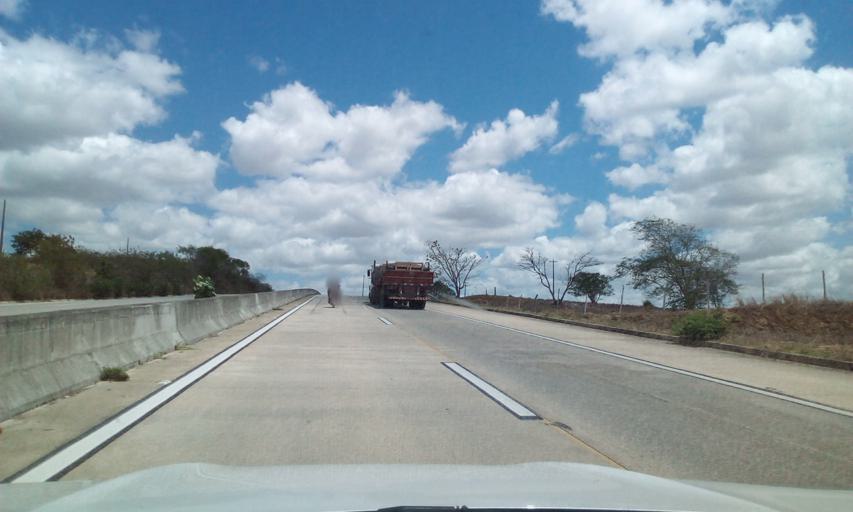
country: BR
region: Alagoas
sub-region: Porto Real Do Colegio
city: Porto Real do Colegio
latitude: -10.1384
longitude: -36.8025
